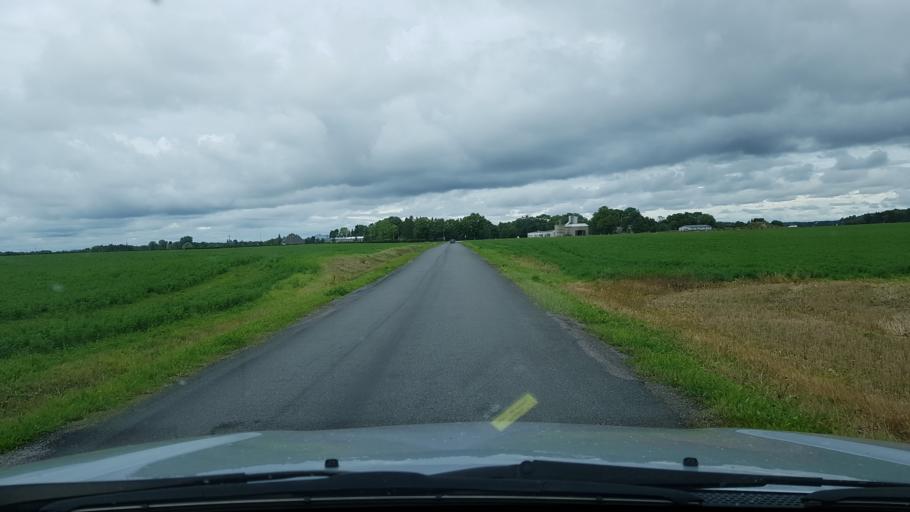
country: EE
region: Harju
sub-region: Rae vald
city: Vaida
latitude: 59.3573
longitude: 24.9650
